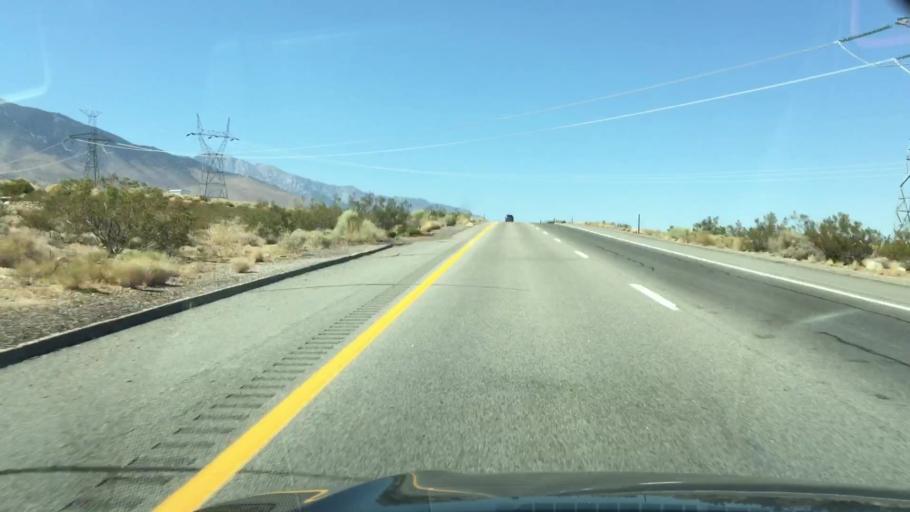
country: US
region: California
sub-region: Kern County
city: Inyokern
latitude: 36.1065
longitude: -117.9686
